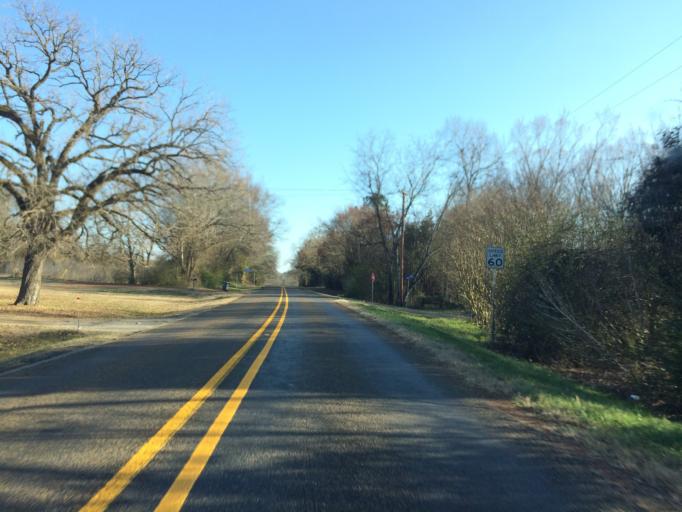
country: US
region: Texas
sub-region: Wood County
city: Quitman
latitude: 32.7145
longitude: -95.3655
